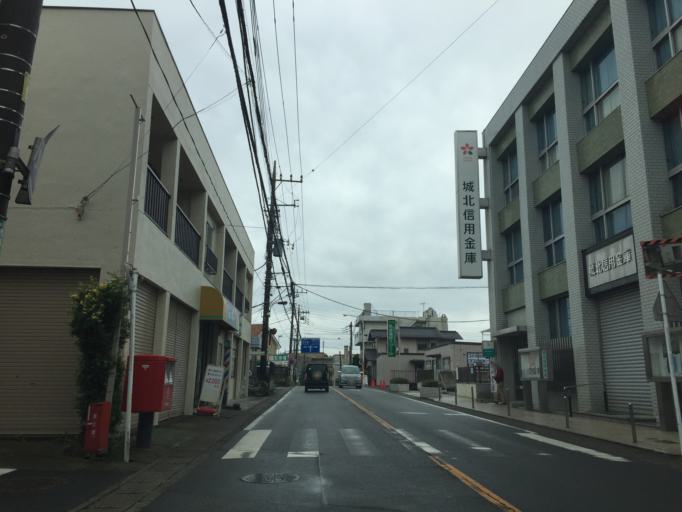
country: JP
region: Saitama
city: Yono
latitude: 35.8630
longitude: 139.6299
